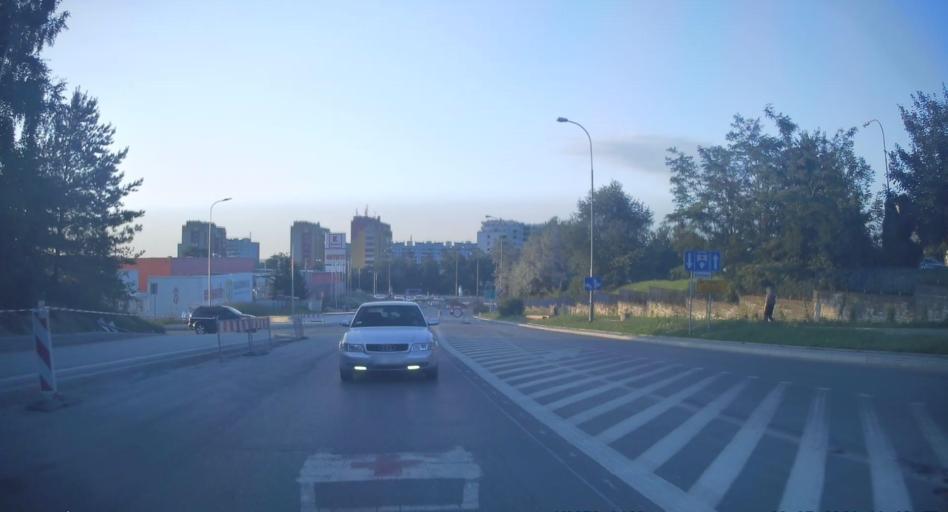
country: PL
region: Lesser Poland Voivodeship
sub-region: Powiat krakowski
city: Ochojno
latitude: 50.0124
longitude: 19.9985
